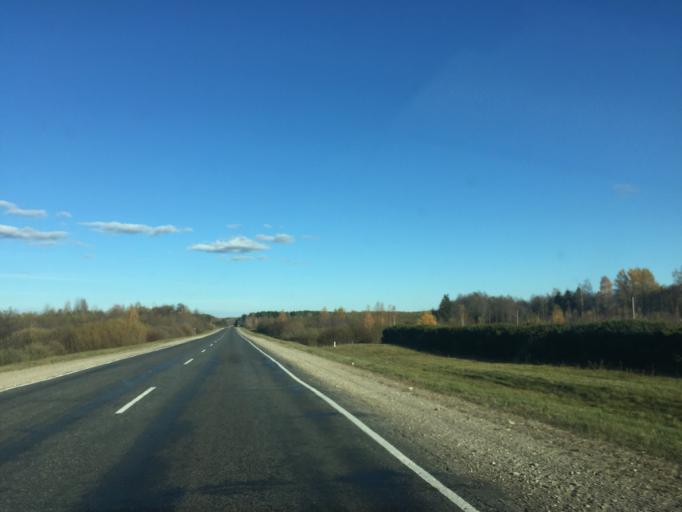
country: BY
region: Vitebsk
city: Dzisna
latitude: 55.2421
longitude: 28.0736
